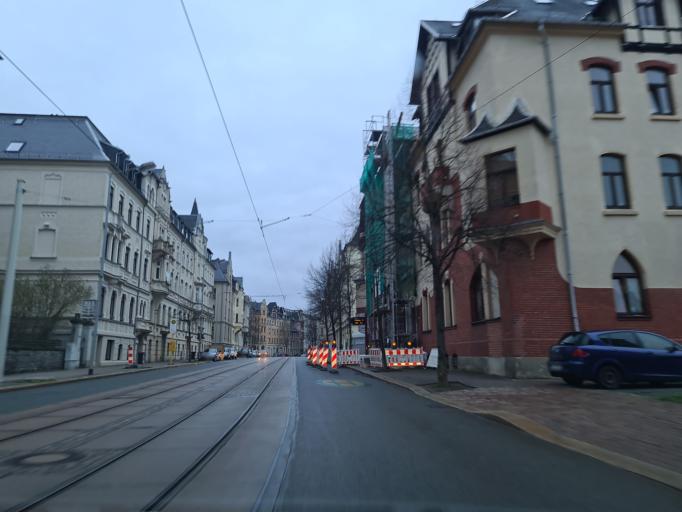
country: DE
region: Saxony
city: Plauen
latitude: 50.4928
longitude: 12.1090
